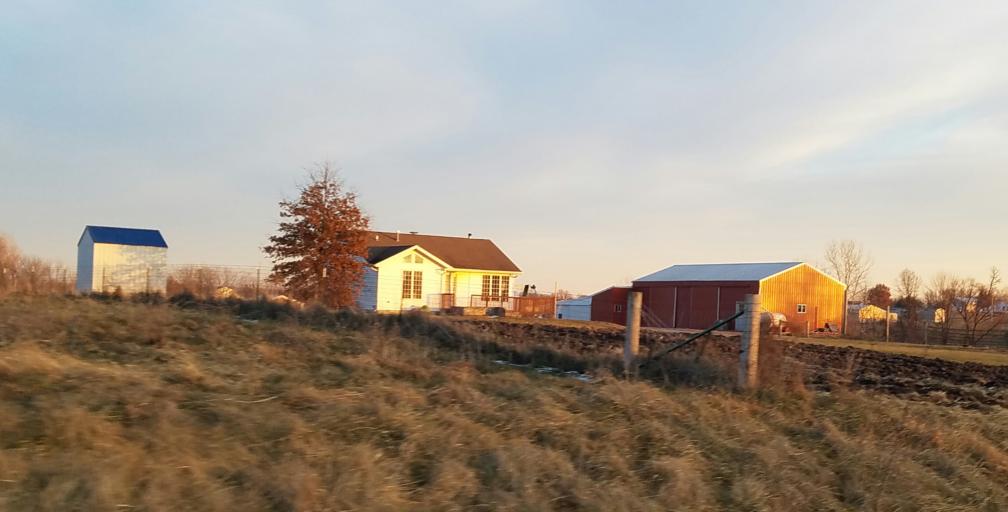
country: US
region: Missouri
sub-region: Boone County
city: Centralia
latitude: 39.2779
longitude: -92.2845
